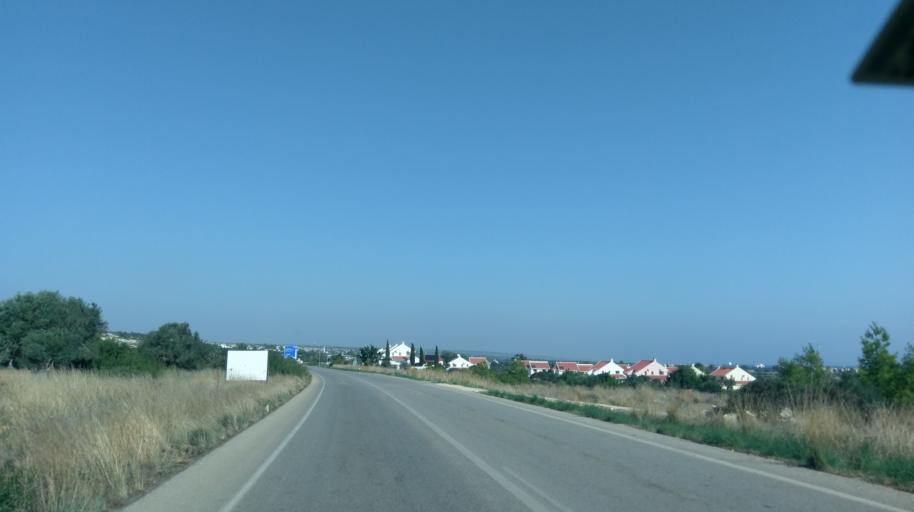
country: CY
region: Ammochostos
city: Leonarisso
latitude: 35.4151
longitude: 34.1188
